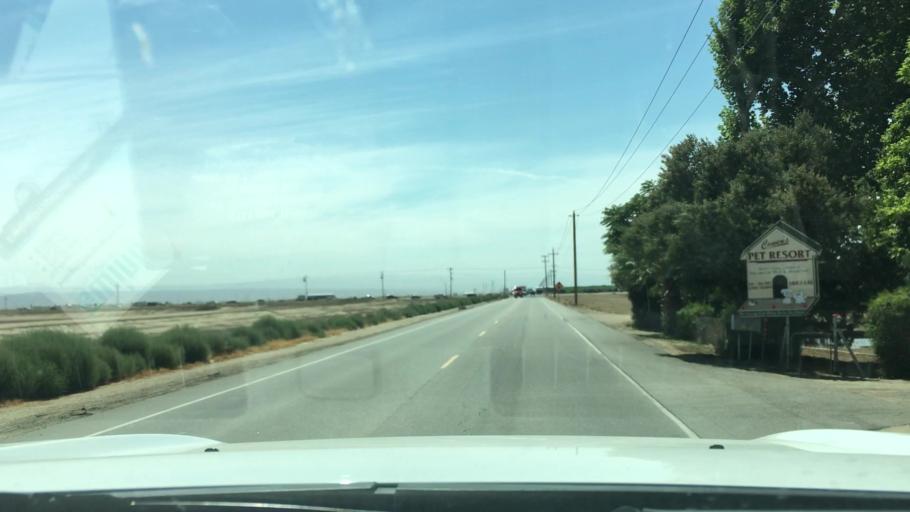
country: US
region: California
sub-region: Kern County
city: Rosedale
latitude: 35.3544
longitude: -119.2477
